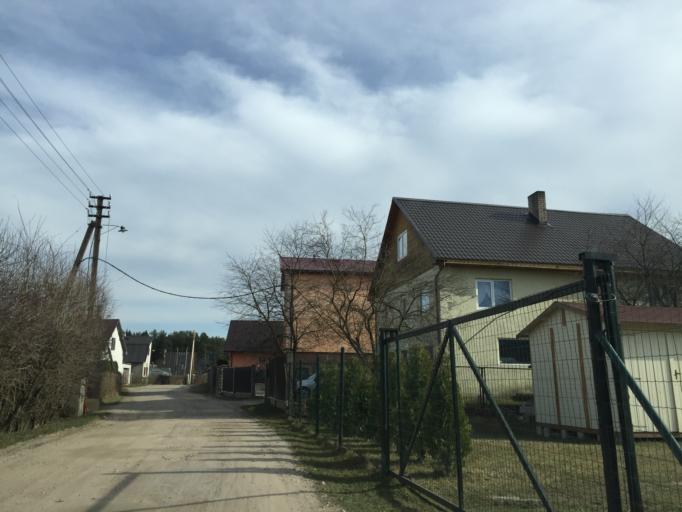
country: LV
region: Ogre
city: Ogre
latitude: 56.8071
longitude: 24.6386
